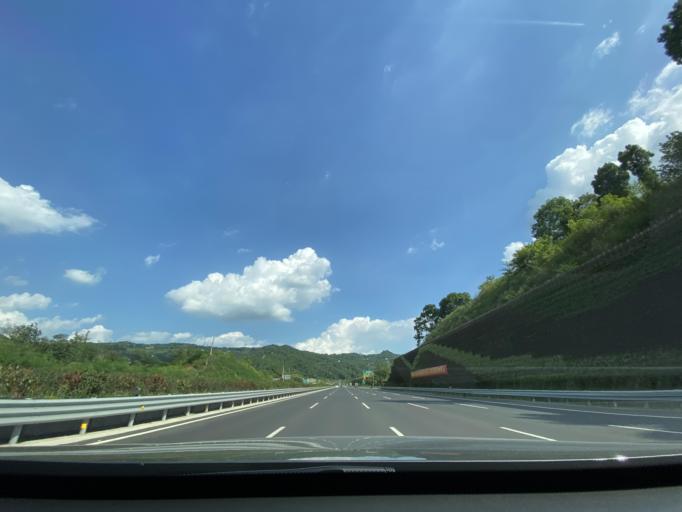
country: CN
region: Sichuan
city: Longquan
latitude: 30.4496
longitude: 104.2374
